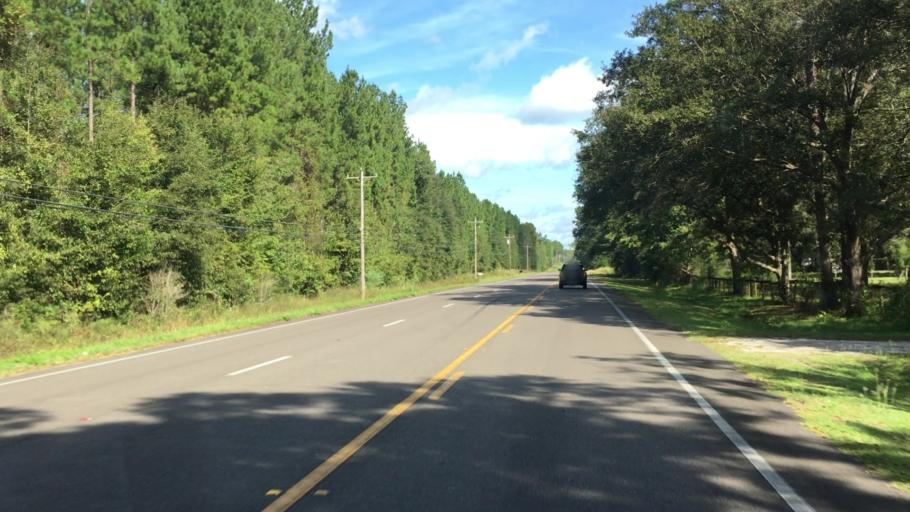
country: US
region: Florida
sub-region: Alachua County
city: Gainesville
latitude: 29.7302
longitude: -82.2768
